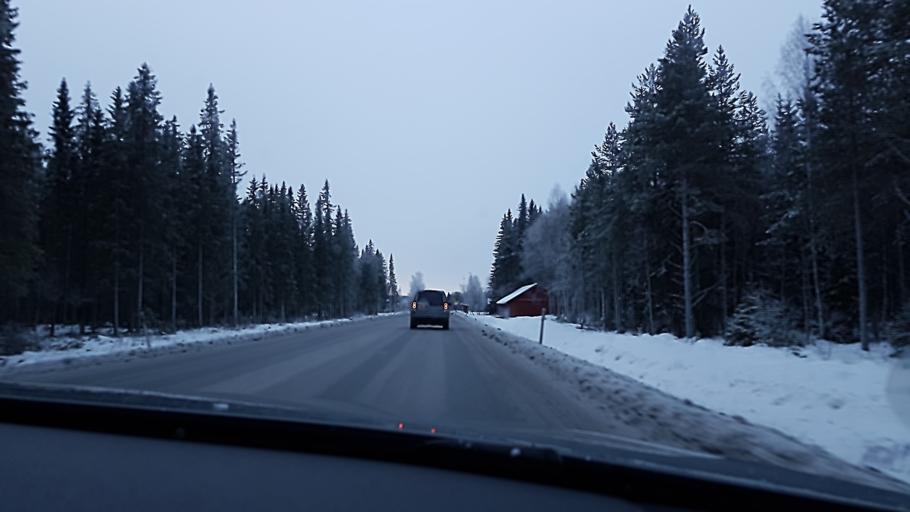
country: SE
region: Jaemtland
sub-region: OEstersunds Kommun
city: Lit
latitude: 63.2837
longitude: 14.8619
